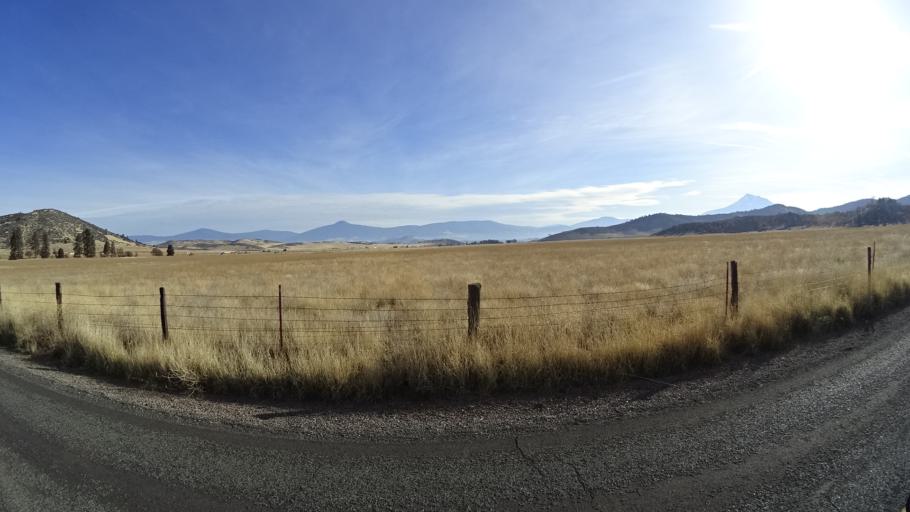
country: US
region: California
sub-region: Siskiyou County
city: Montague
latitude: 41.6532
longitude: -122.5830
